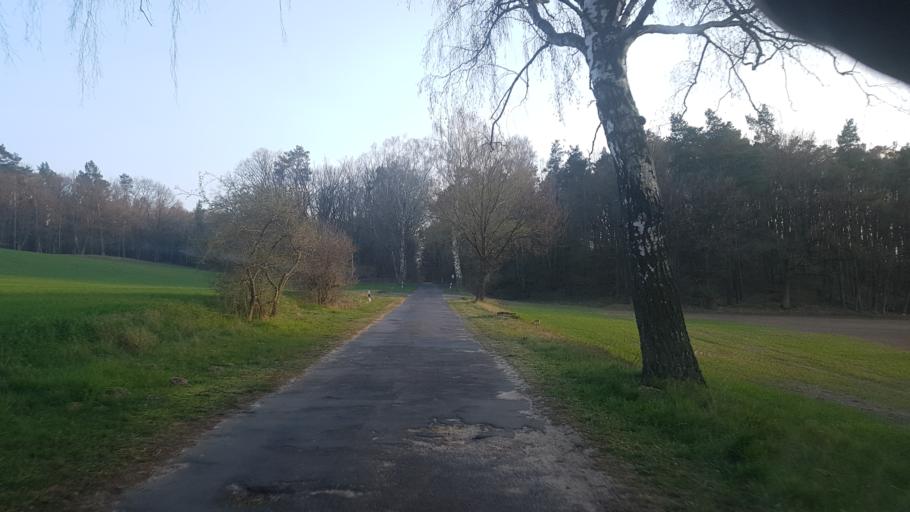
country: DE
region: Brandenburg
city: Gramzow
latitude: 53.2110
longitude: 13.9378
